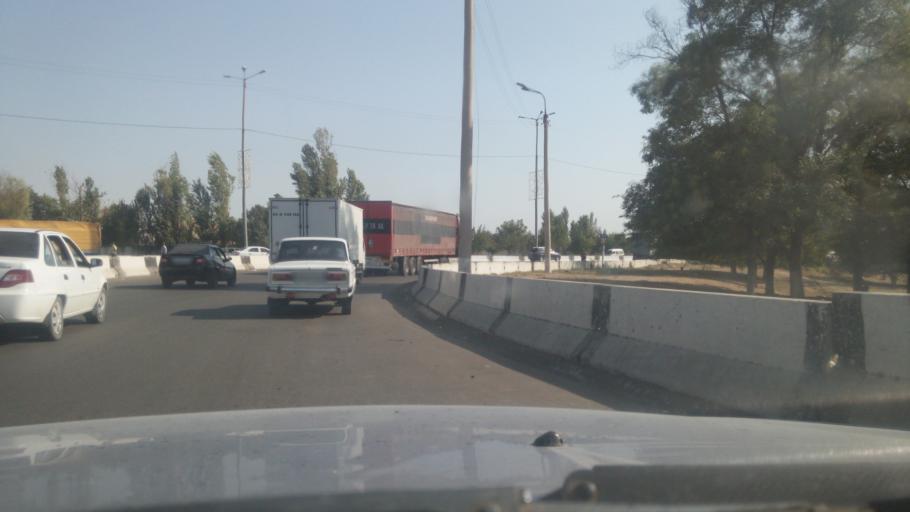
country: UZ
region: Toshkent Shahri
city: Tashkent
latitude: 41.2408
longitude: 69.1689
